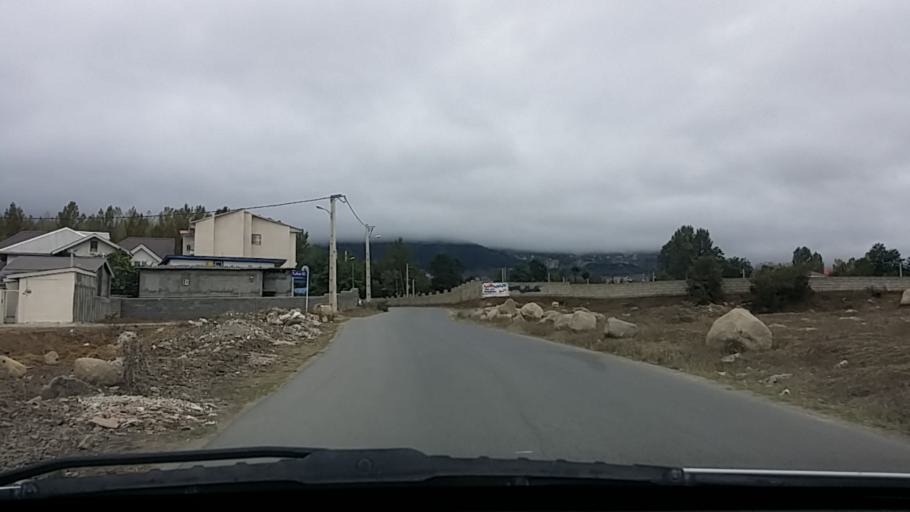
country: IR
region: Mazandaran
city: `Abbasabad
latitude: 36.5175
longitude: 51.1685
